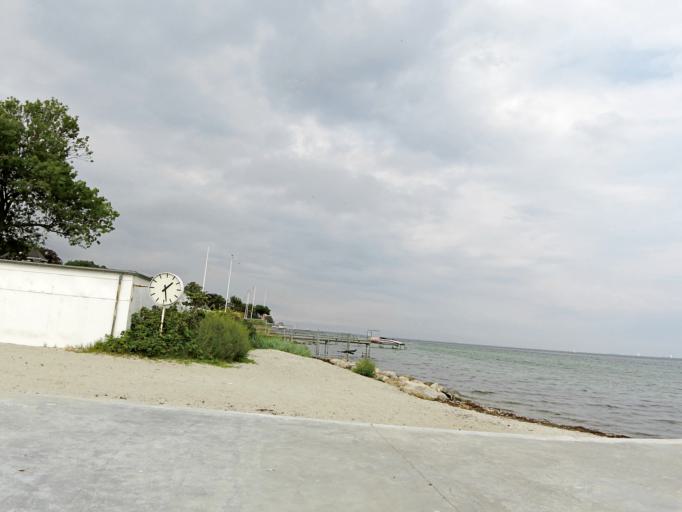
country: DK
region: Capital Region
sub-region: Gentofte Kommune
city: Charlottenlund
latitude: 55.7799
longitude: 12.5930
